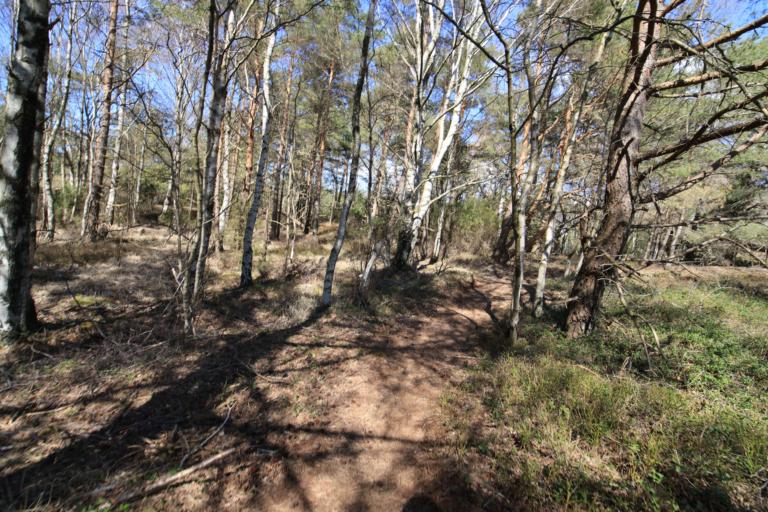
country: SE
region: Halland
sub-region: Varbergs Kommun
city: Varberg
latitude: 57.1754
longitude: 12.2373
